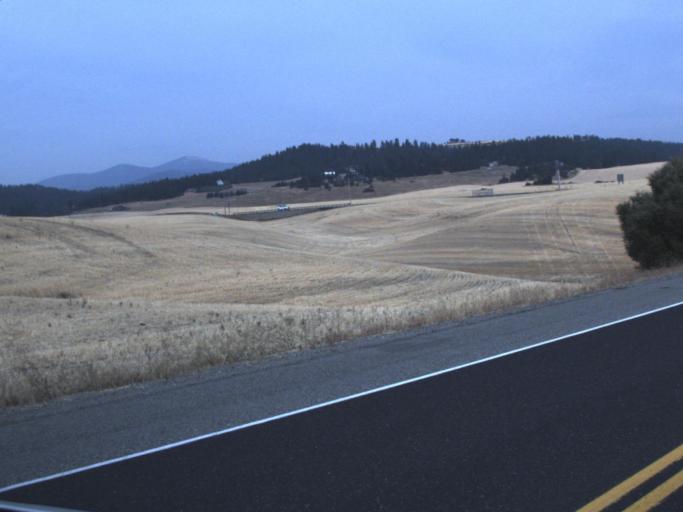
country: US
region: Washington
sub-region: Spokane County
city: Mead
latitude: 47.7875
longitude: -117.3085
